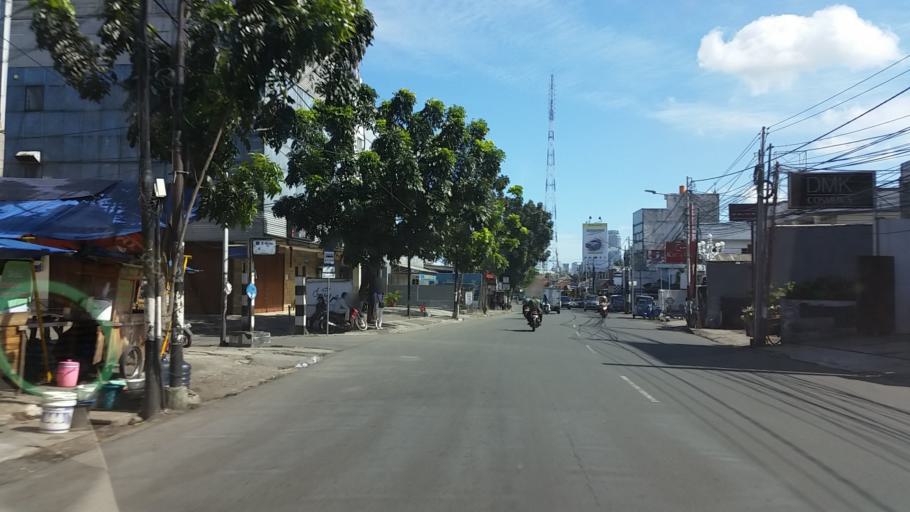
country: ID
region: Jakarta Raya
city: Jakarta
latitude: -6.2556
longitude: 106.7903
